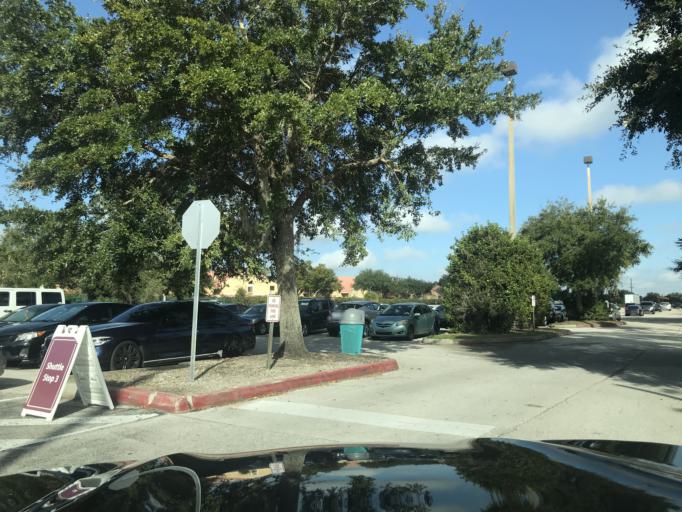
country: US
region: Florida
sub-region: Polk County
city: Citrus Ridge
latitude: 28.3298
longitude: -81.5929
